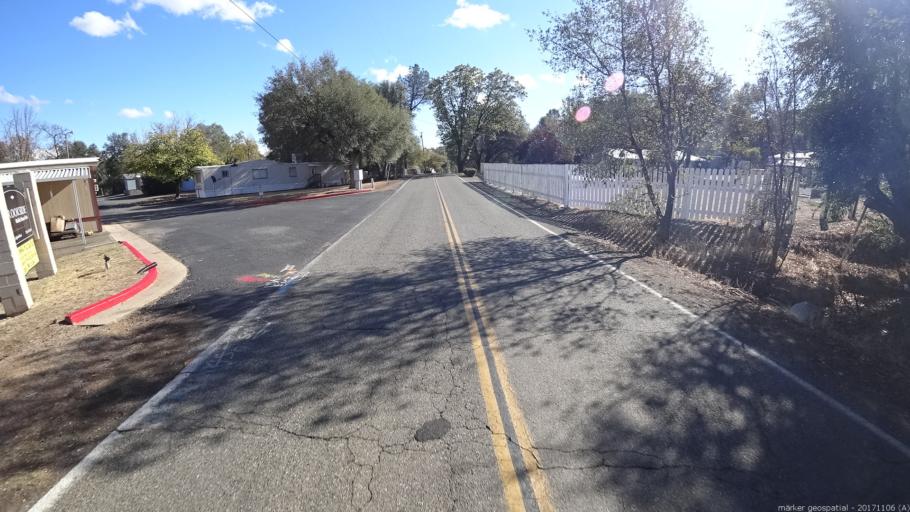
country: US
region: California
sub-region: Shasta County
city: Palo Cedro
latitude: 40.5815
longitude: -122.3022
